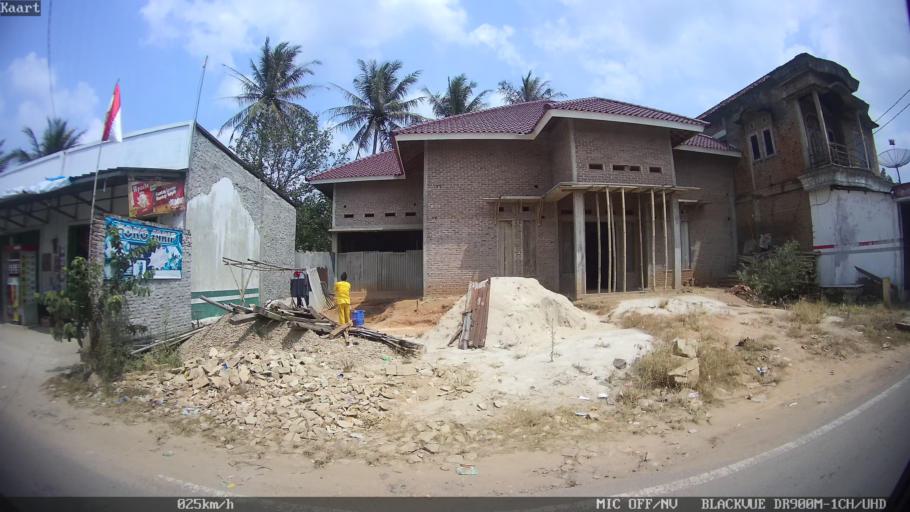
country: ID
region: Lampung
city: Pringsewu
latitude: -5.3695
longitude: 104.9666
